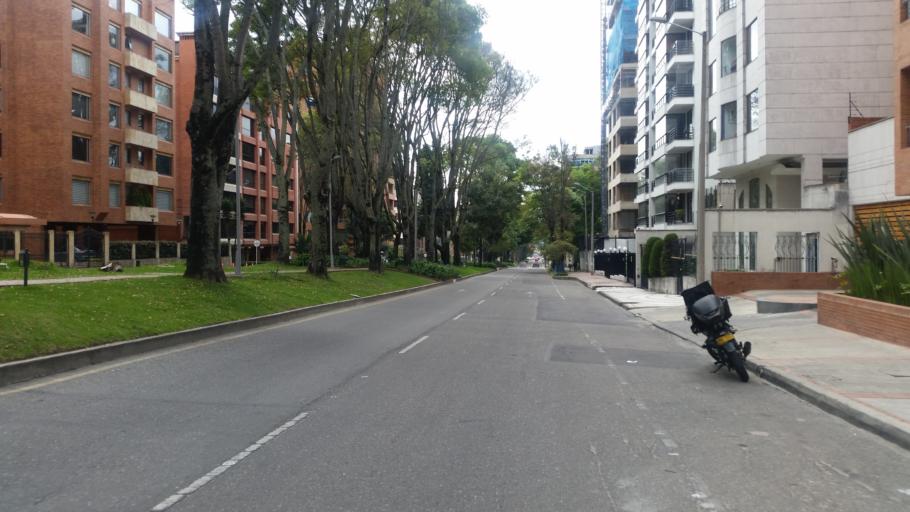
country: CO
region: Bogota D.C.
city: Barrio San Luis
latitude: 4.6763
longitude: -74.0443
